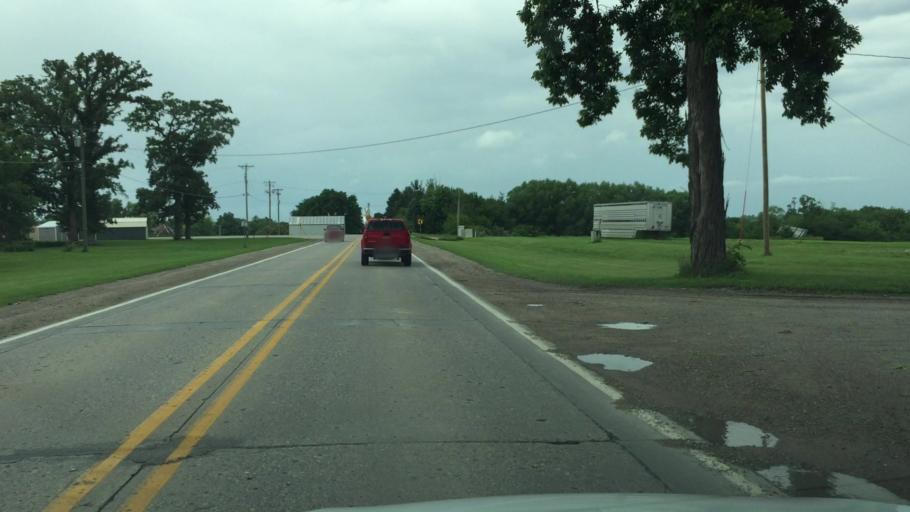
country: US
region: Iowa
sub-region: Jasper County
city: Newton
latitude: 41.7190
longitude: -93.0579
